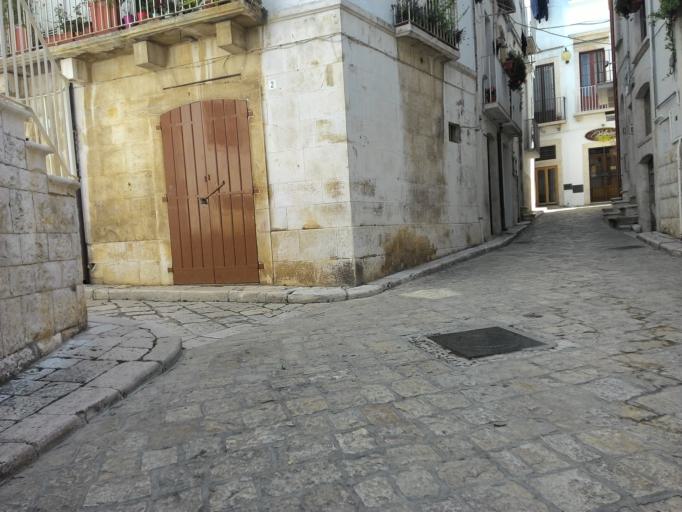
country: IT
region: Apulia
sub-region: Provincia di Bari
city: Putignano
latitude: 40.8496
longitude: 17.1215
